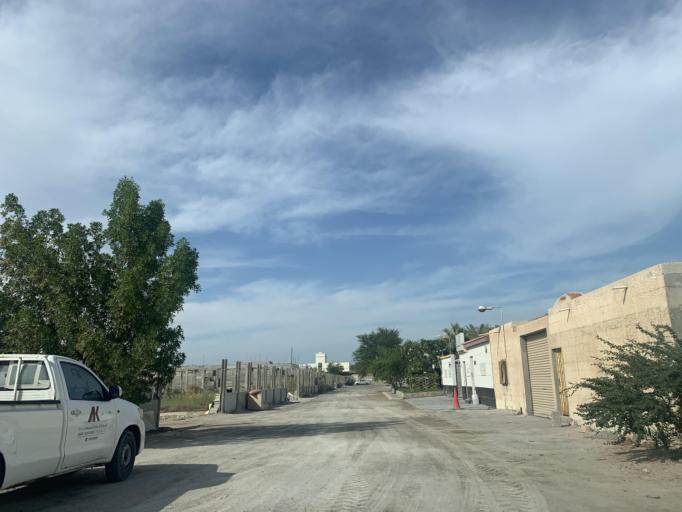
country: BH
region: Central Governorate
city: Madinat Hamad
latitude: 26.1225
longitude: 50.4695
